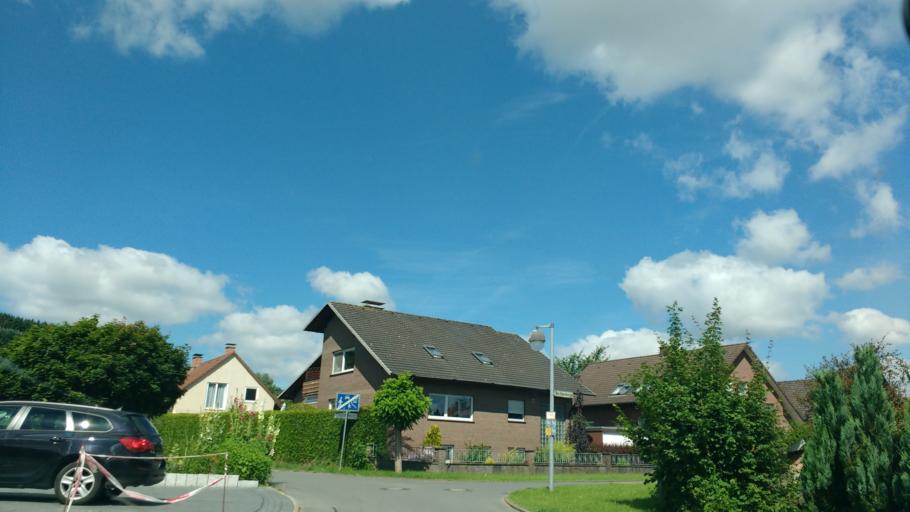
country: DE
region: Lower Saxony
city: Bad Pyrmont
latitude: 51.9786
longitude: 9.2290
